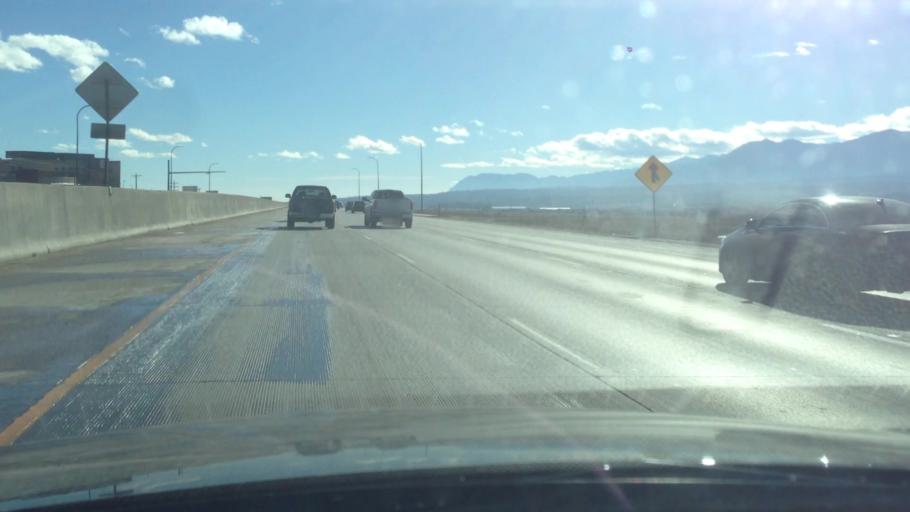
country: US
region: Colorado
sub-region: El Paso County
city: Monument
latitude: 39.0851
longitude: -104.8610
